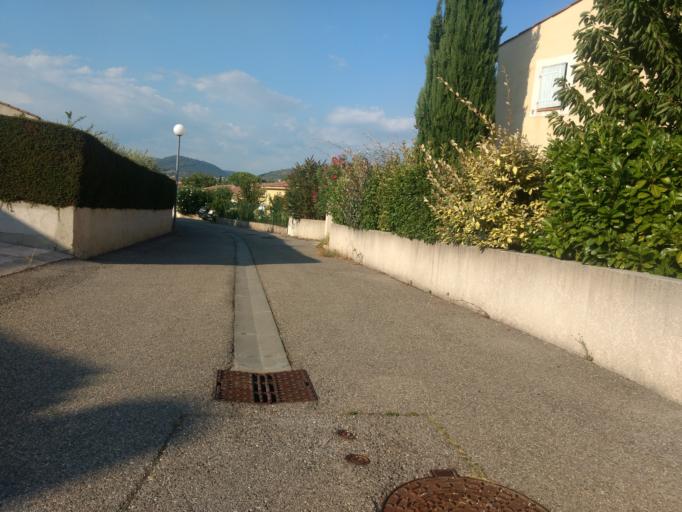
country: FR
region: Provence-Alpes-Cote d'Azur
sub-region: Departement des Alpes-de-Haute-Provence
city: Manosque
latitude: 43.8190
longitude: 5.7744
